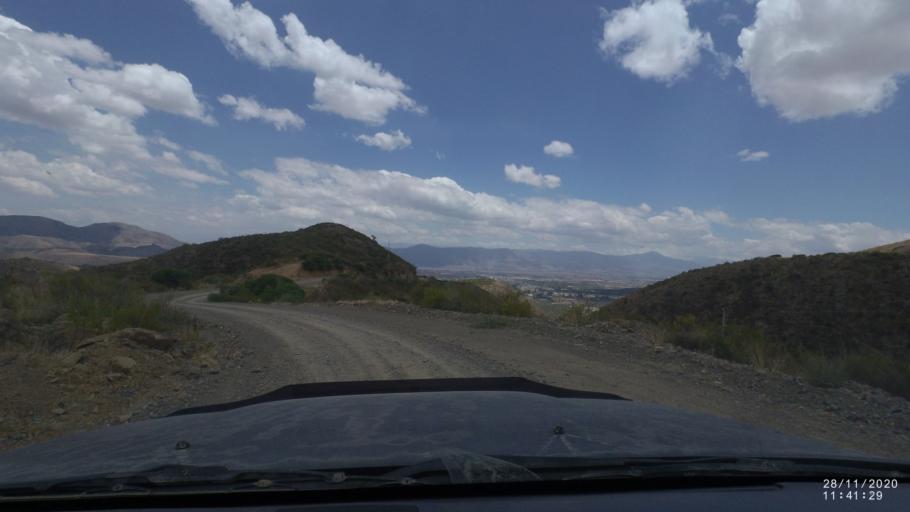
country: BO
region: Cochabamba
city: Tarata
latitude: -17.6697
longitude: -66.0482
